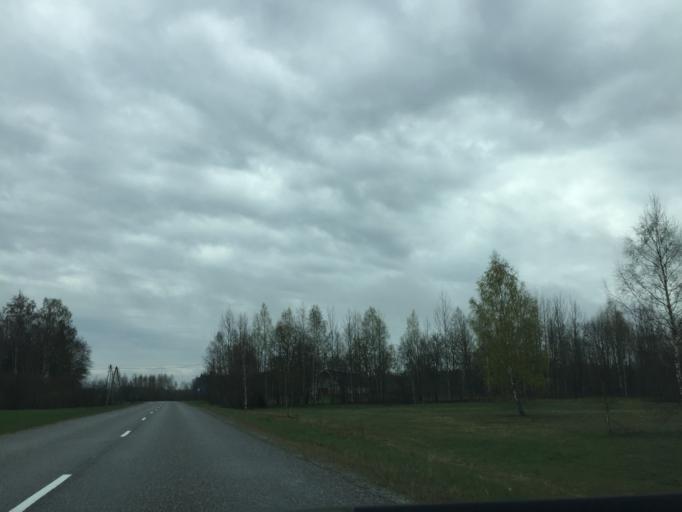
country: LV
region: Malpils
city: Malpils
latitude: 57.0115
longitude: 24.8954
